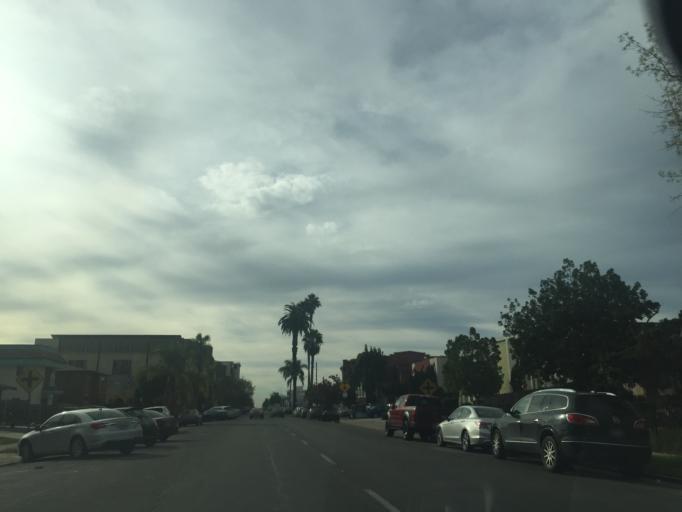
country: US
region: California
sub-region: San Diego County
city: San Diego
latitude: 32.7527
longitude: -117.1020
